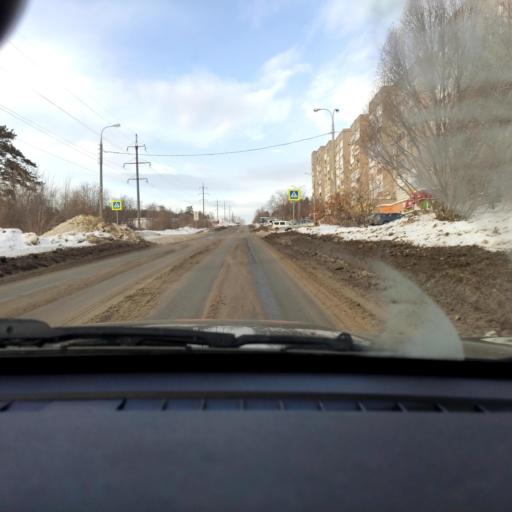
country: RU
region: Samara
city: Pribrezhnyy
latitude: 53.4893
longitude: 49.8470
